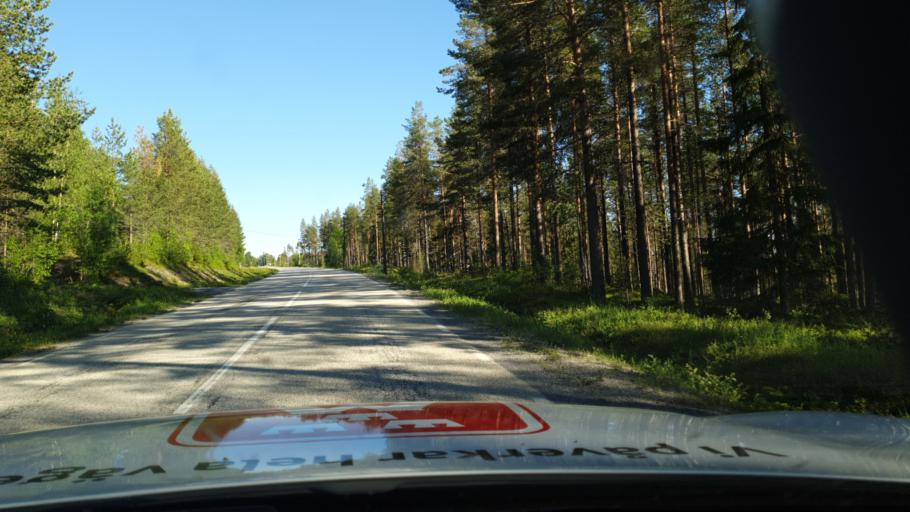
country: SE
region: Jaemtland
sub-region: Bergs Kommun
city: Hoverberg
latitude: 62.6974
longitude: 14.2667
